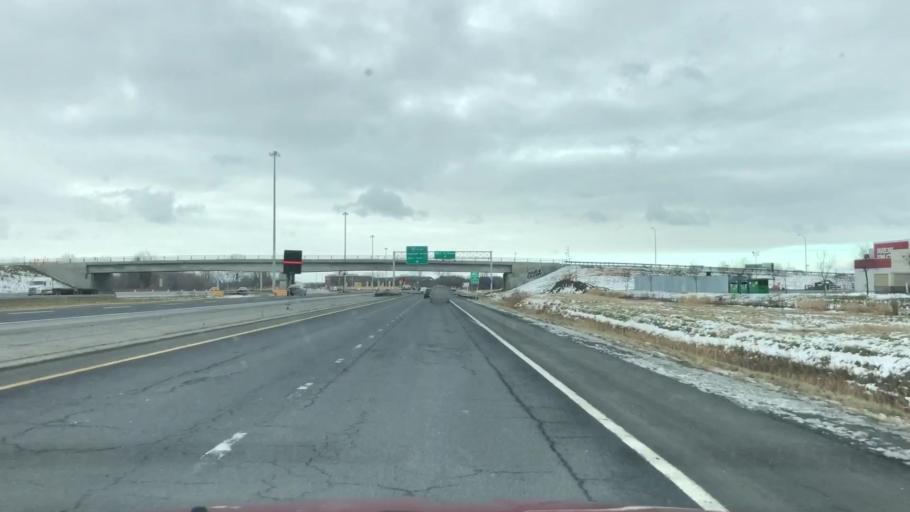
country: CA
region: Quebec
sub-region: Monteregie
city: Brossard
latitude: 45.4395
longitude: -73.4358
